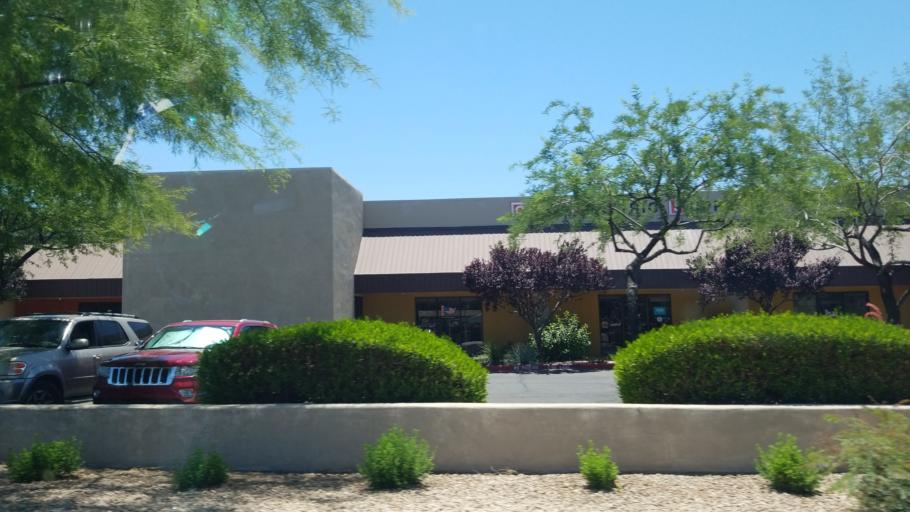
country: US
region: Arizona
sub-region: Maricopa County
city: Paradise Valley
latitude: 33.6177
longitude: -111.9124
